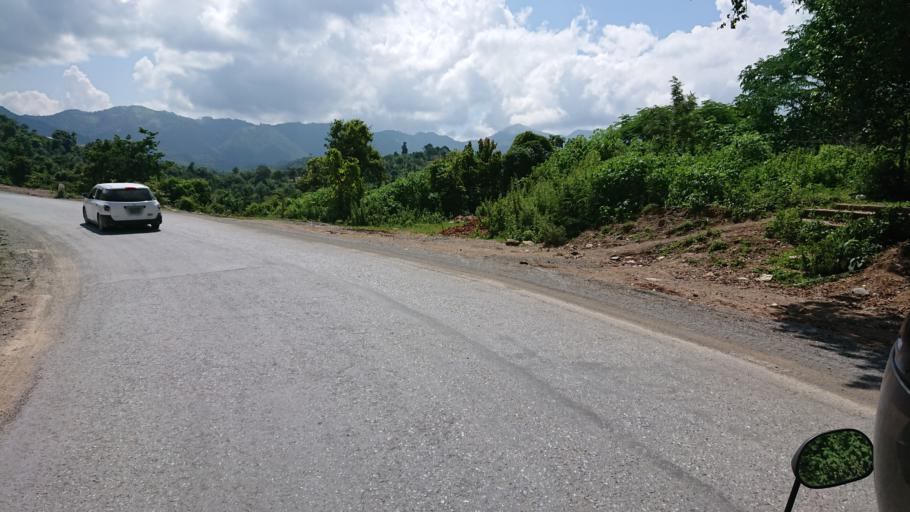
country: MM
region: Shan
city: Taunggyi
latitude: 20.8132
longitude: 97.3179
